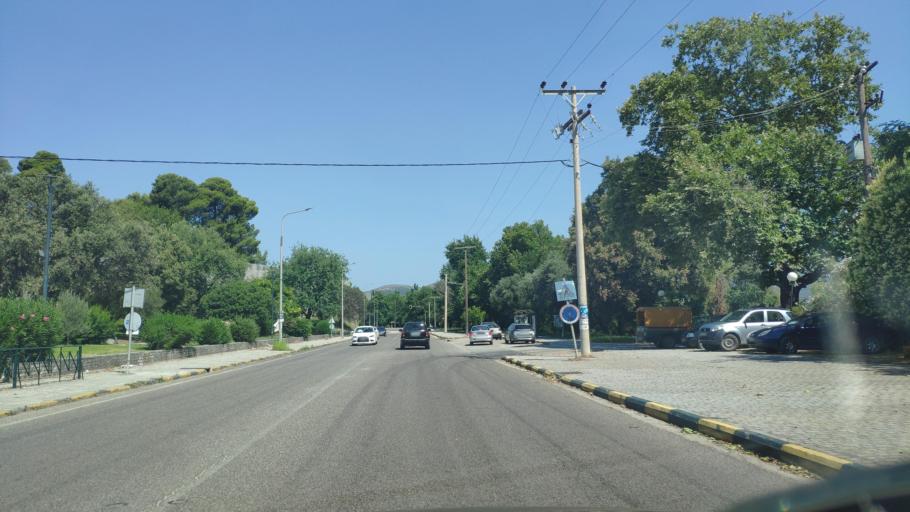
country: GR
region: Epirus
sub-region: Nomos Artas
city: Arta
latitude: 39.1650
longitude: 20.9903
